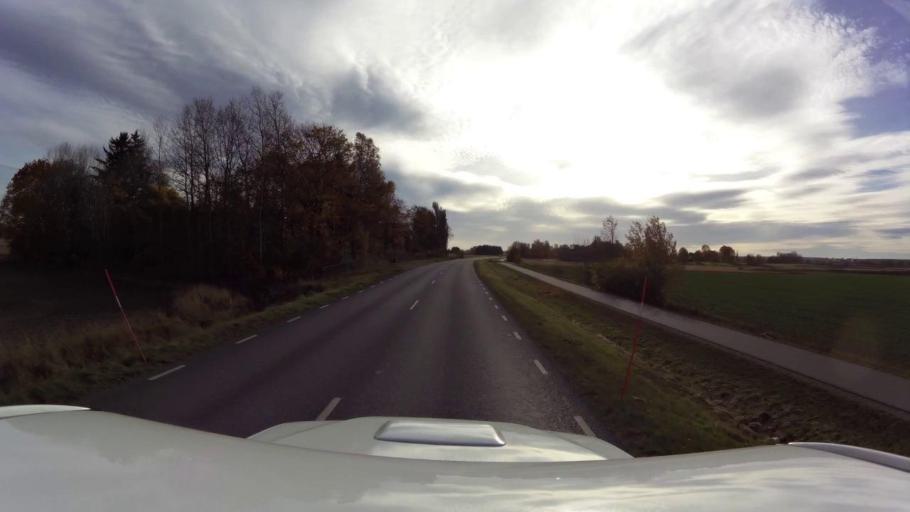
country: SE
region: OEstergoetland
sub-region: Linkopings Kommun
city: Ekangen
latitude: 58.4501
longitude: 15.6444
